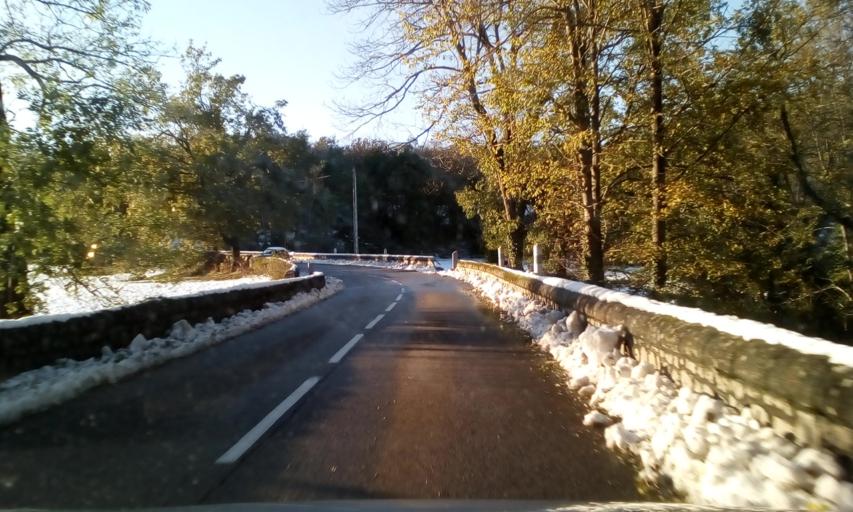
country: FR
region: Rhone-Alpes
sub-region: Departement de l'Ardeche
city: Quintenas
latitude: 45.1562
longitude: 4.6963
